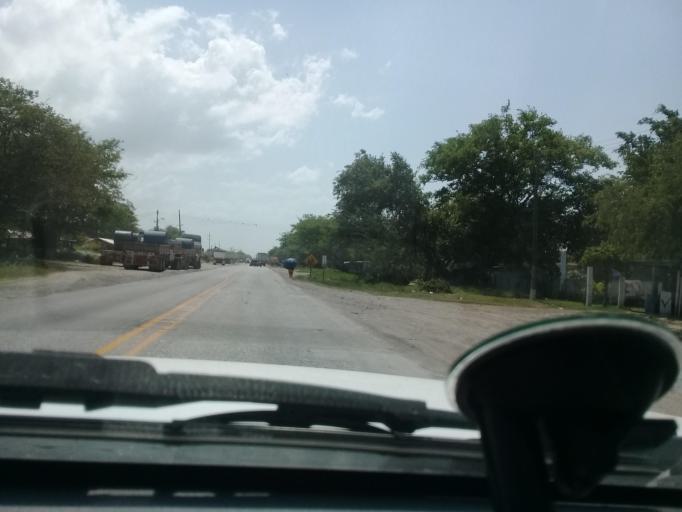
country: MX
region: Veracruz
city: Moralillo
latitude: 22.1715
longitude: -98.0486
